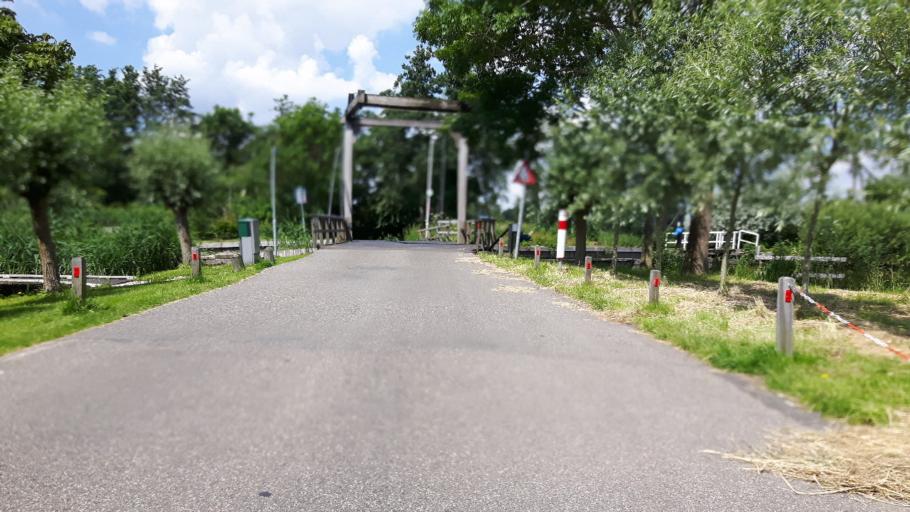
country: NL
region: South Holland
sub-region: Bodegraven-Reeuwijk
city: Reeuwijk
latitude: 52.0367
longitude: 4.7494
